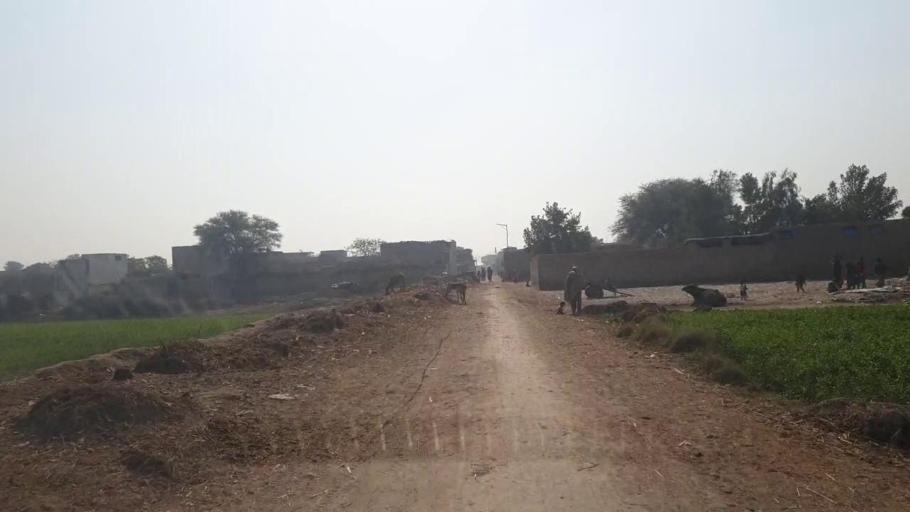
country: PK
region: Sindh
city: Tando Allahyar
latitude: 25.3637
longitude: 68.6485
